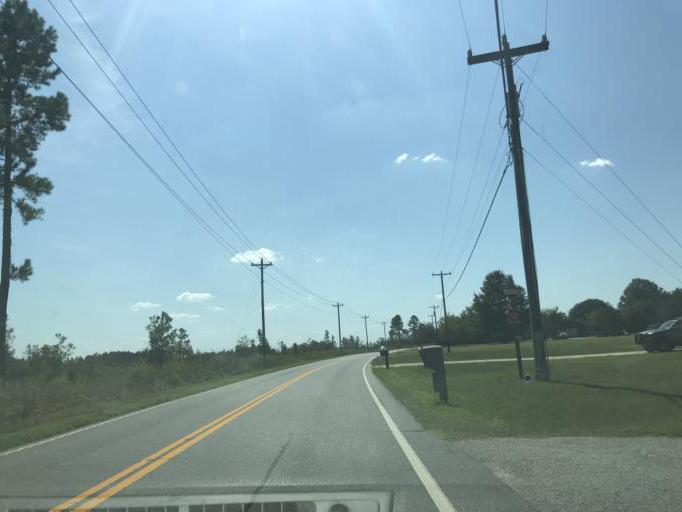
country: US
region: South Carolina
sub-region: Cherokee County
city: Gaffney
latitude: 35.1032
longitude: -81.7052
